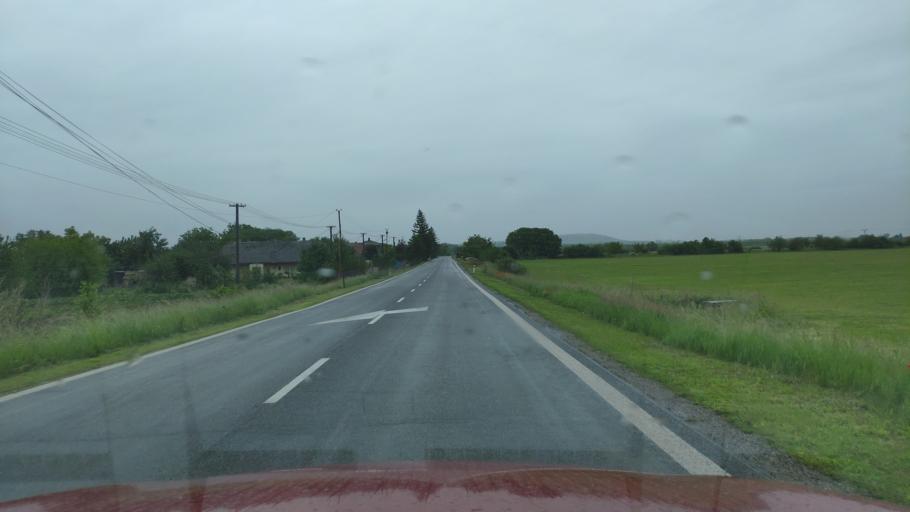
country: HU
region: Borsod-Abauj-Zemplen
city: Karcsa
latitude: 48.4350
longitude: 21.8647
